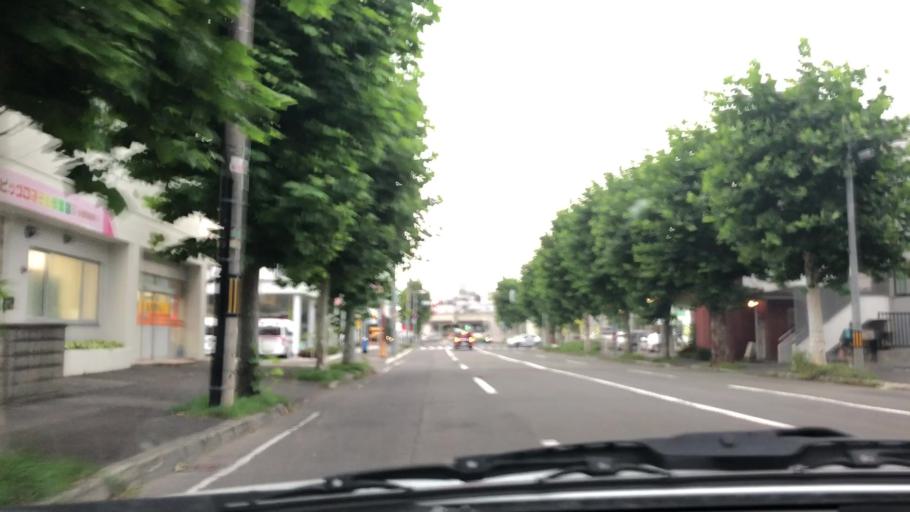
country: JP
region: Hokkaido
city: Sapporo
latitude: 43.0700
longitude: 141.3287
